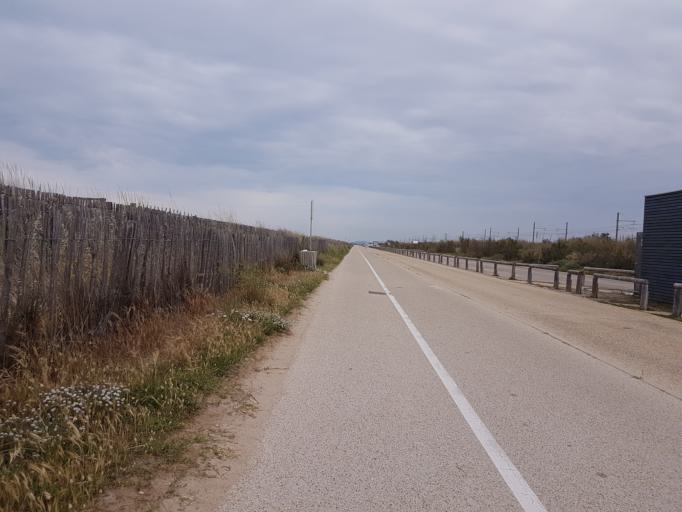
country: FR
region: Languedoc-Roussillon
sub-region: Departement de l'Herault
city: Sete
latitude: 43.3842
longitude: 3.6427
